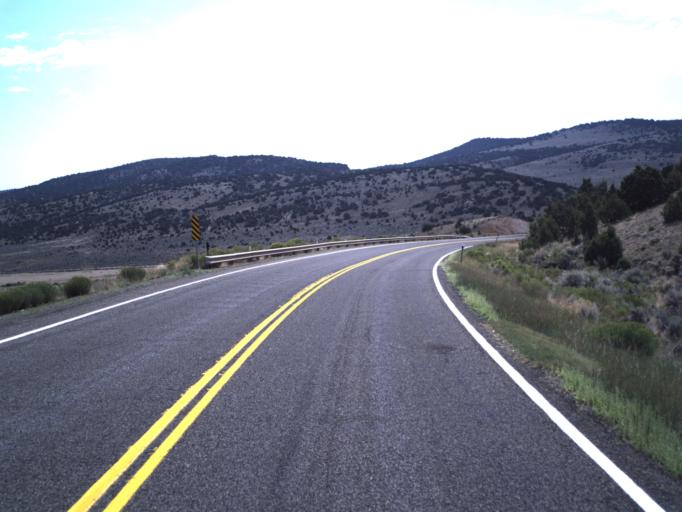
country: US
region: Utah
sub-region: Daggett County
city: Manila
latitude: 40.9389
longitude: -109.7040
